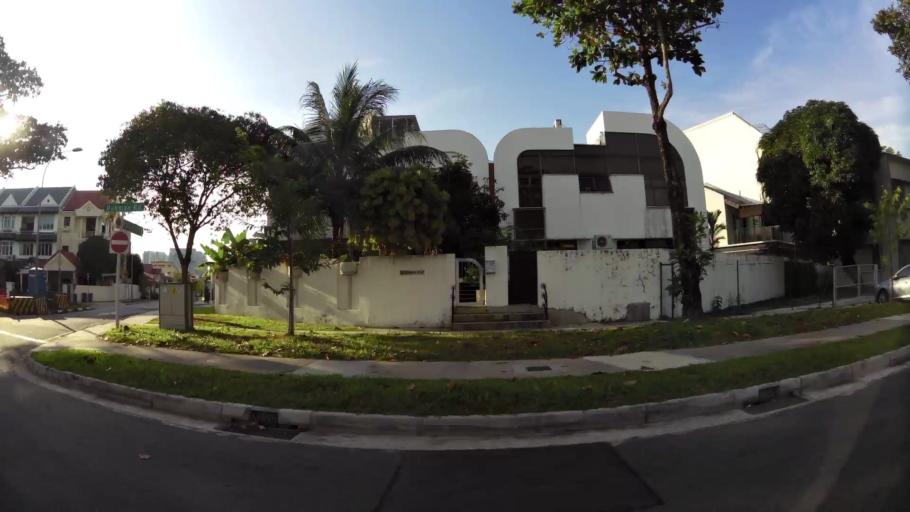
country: SG
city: Singapore
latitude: 1.3094
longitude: 103.9006
